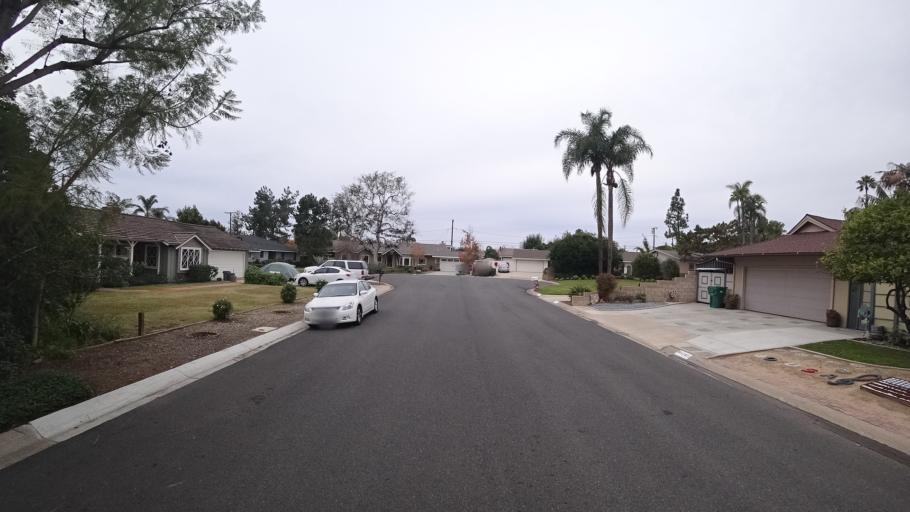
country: US
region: California
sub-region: Orange County
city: North Tustin
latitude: 33.7516
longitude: -117.7990
